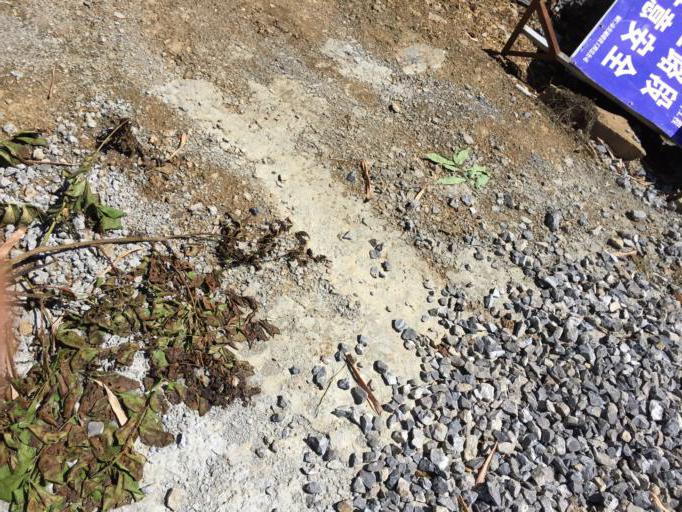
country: CN
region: Guizhou Sheng
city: Shiqian
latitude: 27.6731
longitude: 108.0839
